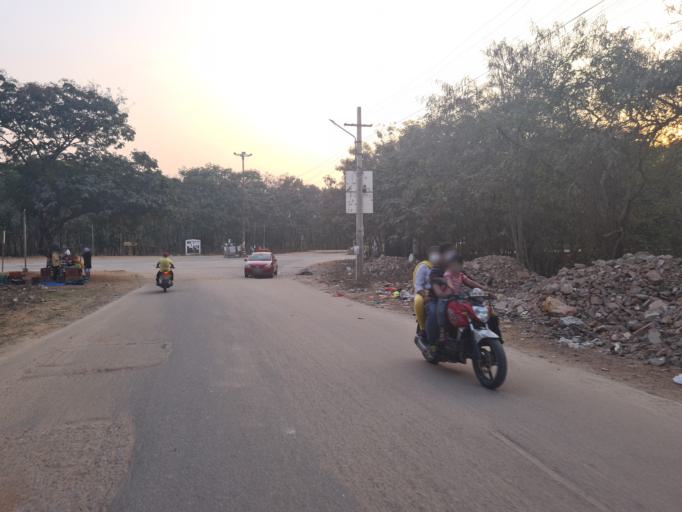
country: IN
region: Telangana
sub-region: Medak
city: Serilingampalle
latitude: 17.4785
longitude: 78.2949
